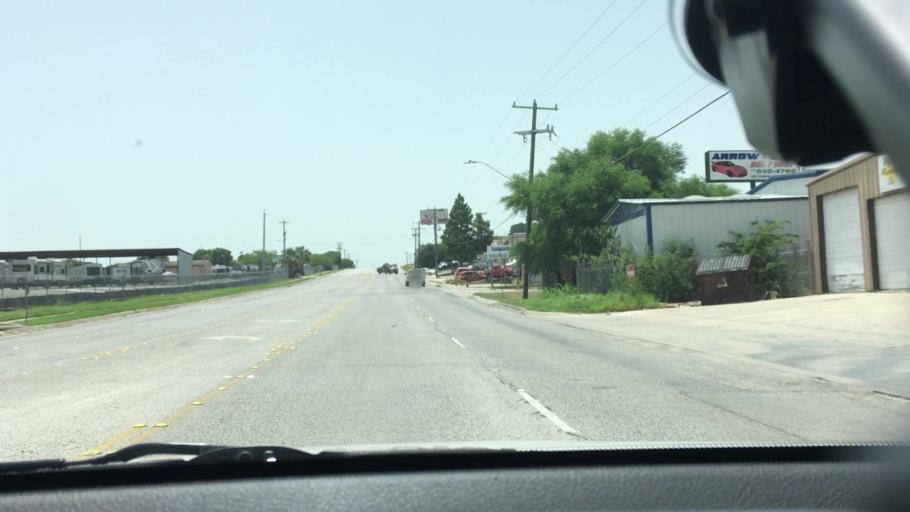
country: US
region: Texas
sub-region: Bexar County
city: Live Oak
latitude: 29.5683
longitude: -98.3554
